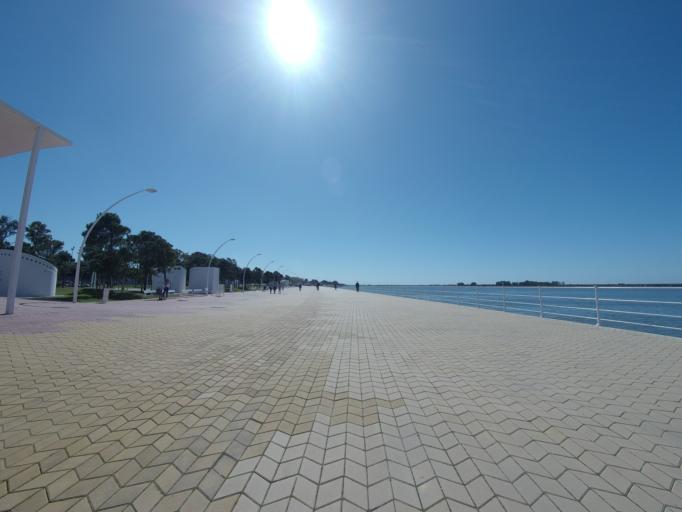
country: ES
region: Andalusia
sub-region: Provincia de Huelva
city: Huelva
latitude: 37.2490
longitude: -6.9576
